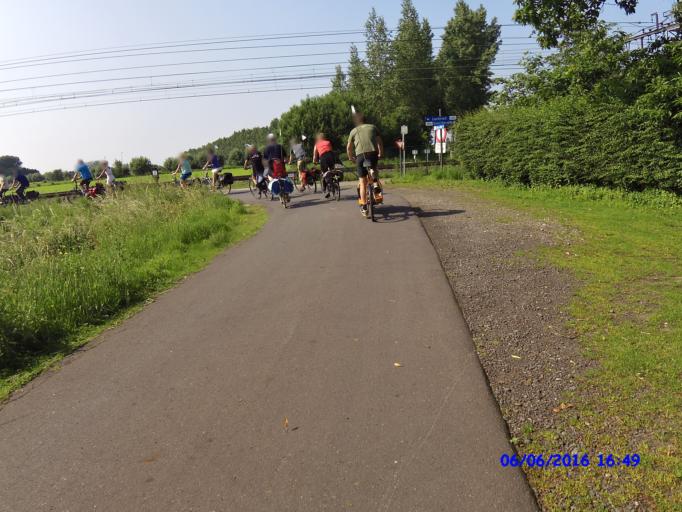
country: BE
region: Flanders
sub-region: Provincie Oost-Vlaanderen
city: Lochristi
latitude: 51.0856
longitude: 3.8729
